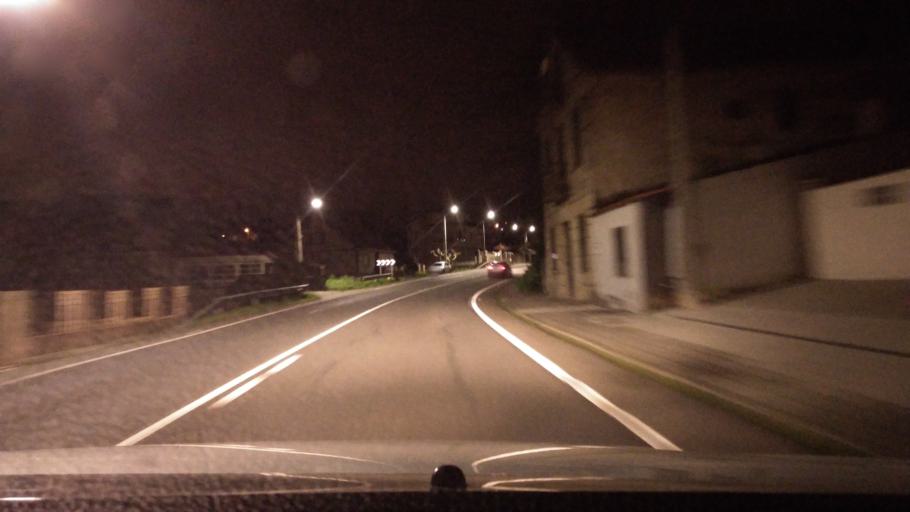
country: ES
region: Galicia
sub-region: Provincia de Pontevedra
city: Moana
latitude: 42.2762
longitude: -8.7435
